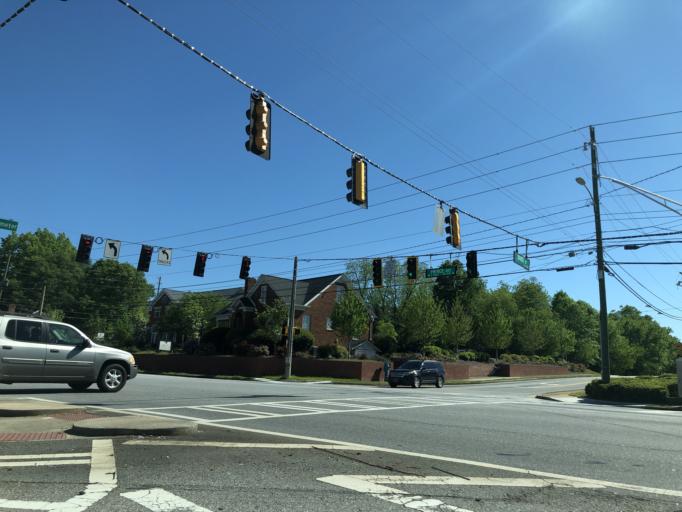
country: US
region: Georgia
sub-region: Clarke County
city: Country Club Estates
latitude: 33.9691
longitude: -83.4085
